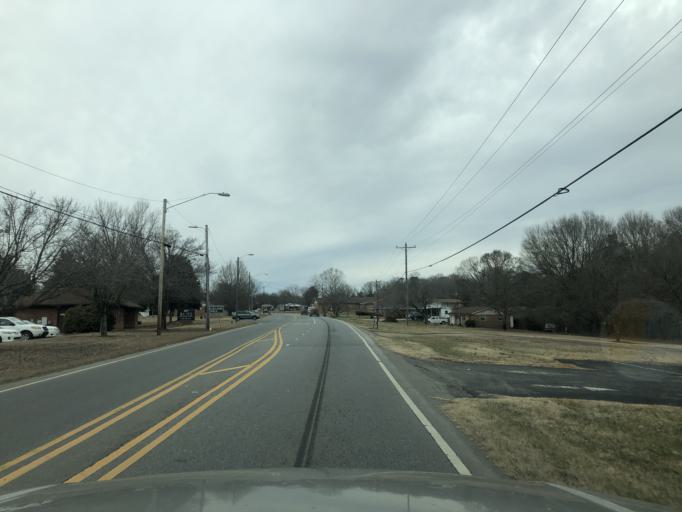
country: US
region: North Carolina
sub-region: Cleveland County
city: Shelby
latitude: 35.2701
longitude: -81.4804
